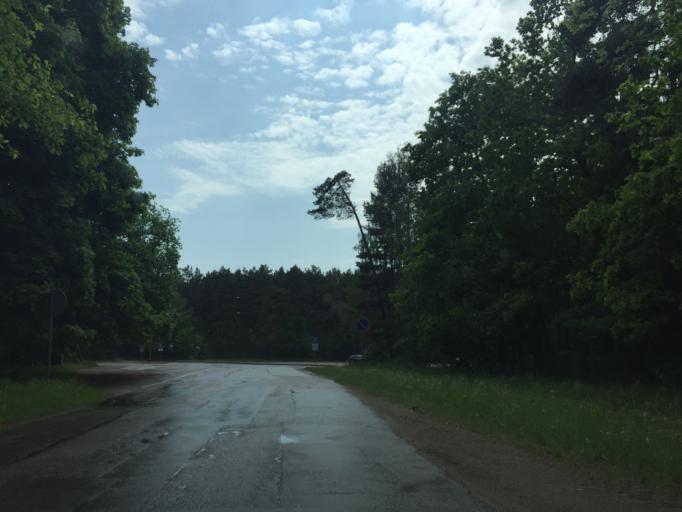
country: LT
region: Klaipedos apskritis
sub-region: Klaipeda
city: Klaipeda
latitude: 55.7723
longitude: 21.0835
